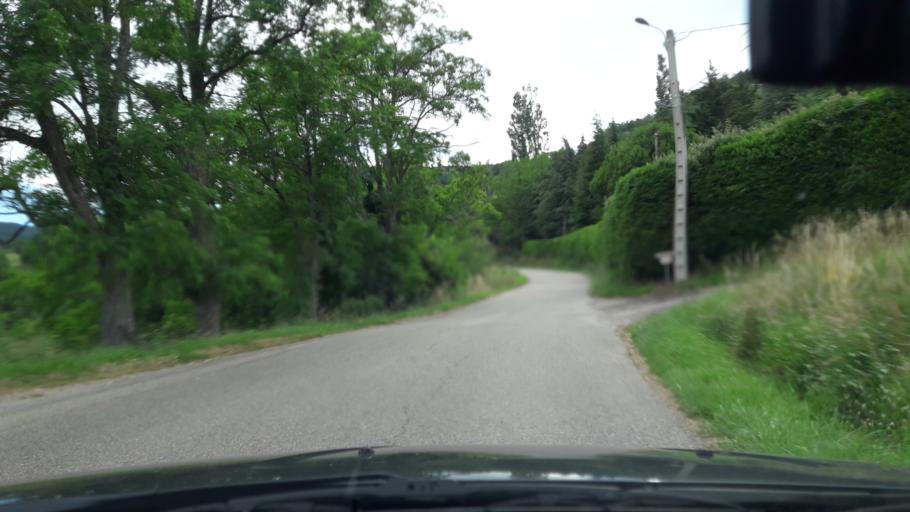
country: FR
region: Rhone-Alpes
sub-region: Departement de l'Ardeche
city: Alissas
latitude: 44.6897
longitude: 4.6349
